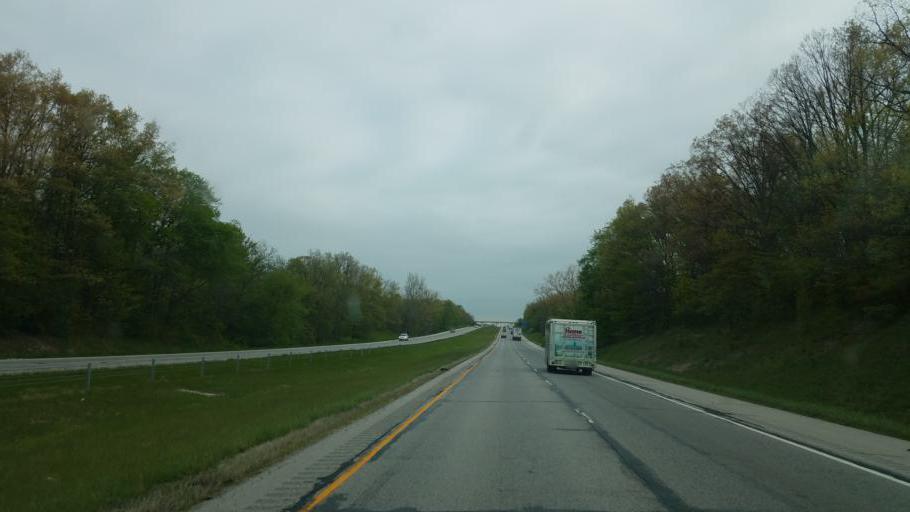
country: US
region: Indiana
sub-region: Allen County
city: Leo-Cedarville
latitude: 41.2715
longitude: -85.0868
